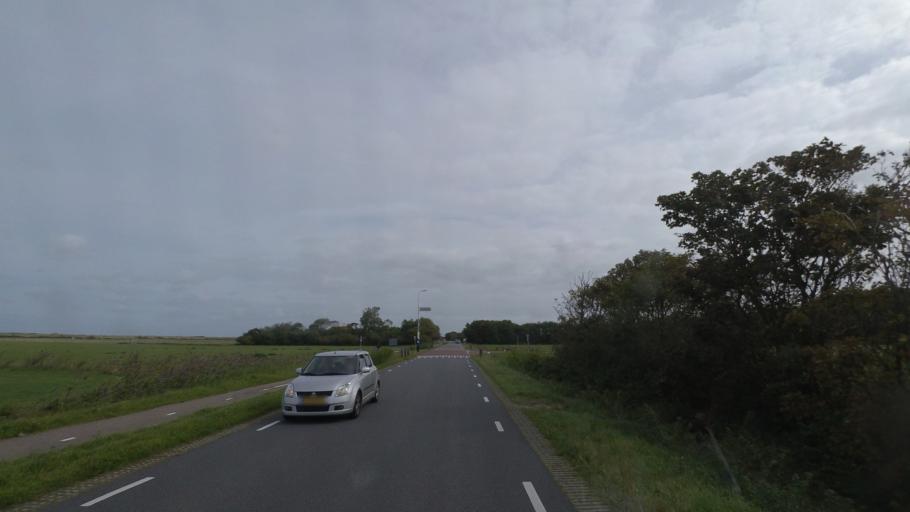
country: NL
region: Friesland
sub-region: Gemeente Ameland
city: Nes
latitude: 53.4454
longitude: 5.7199
